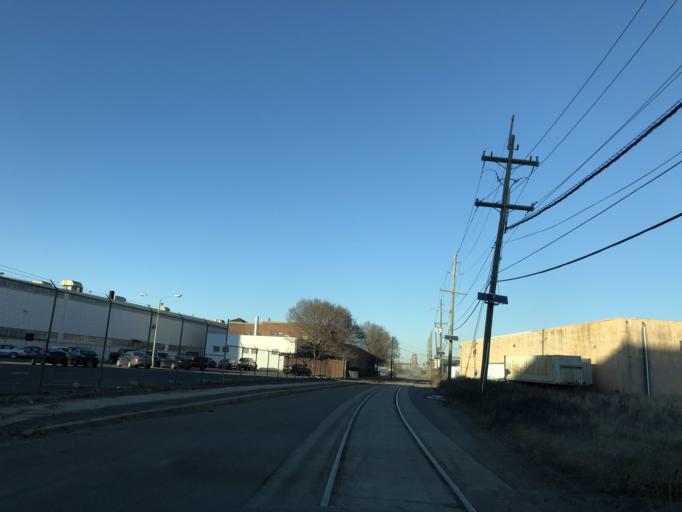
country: US
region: New Jersey
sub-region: Camden County
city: Camden
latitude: 39.9302
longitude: -75.1293
